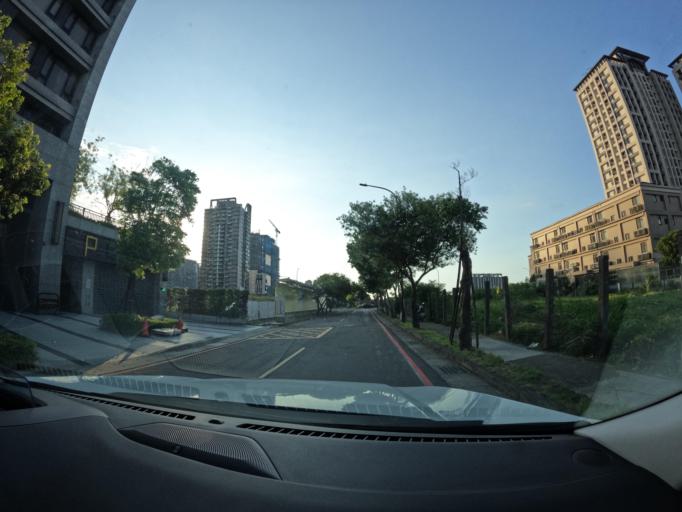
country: TW
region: Taiwan
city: Taoyuan City
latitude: 25.0099
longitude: 121.2109
